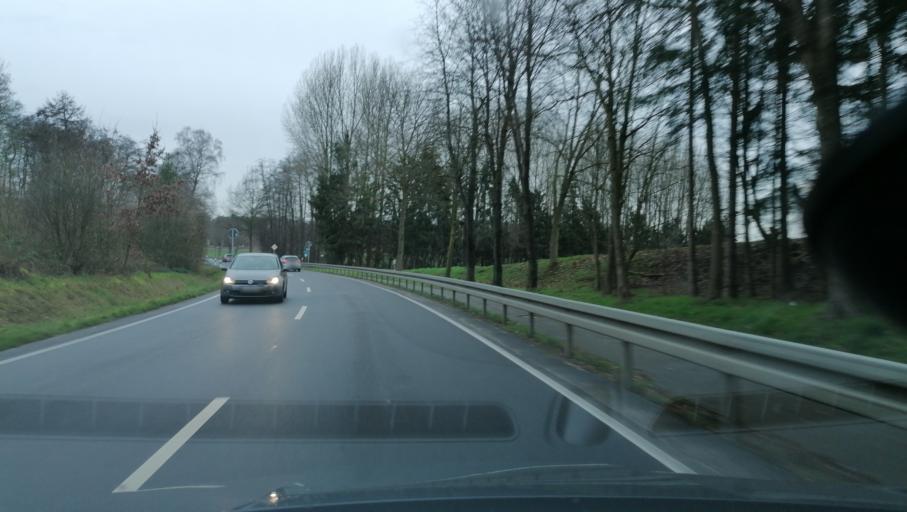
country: DE
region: North Rhine-Westphalia
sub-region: Regierungsbezirk Munster
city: Klein Reken
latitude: 51.8057
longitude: 7.0322
